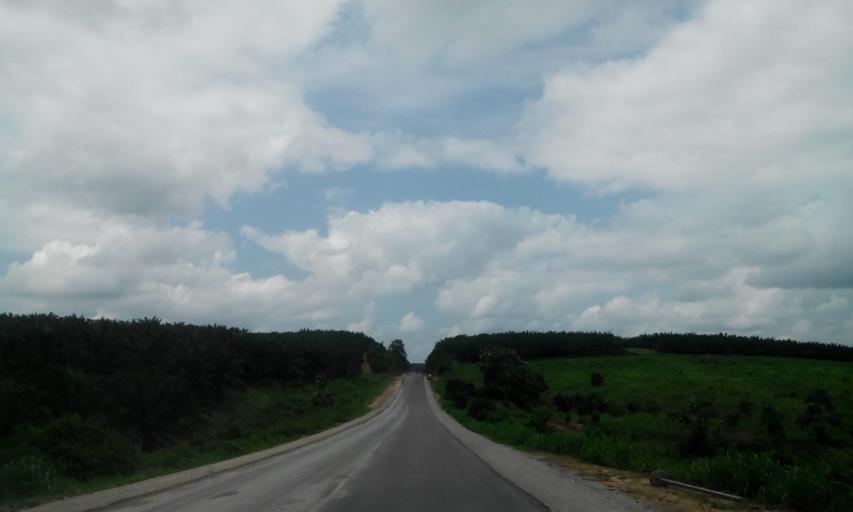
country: CI
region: Sud-Comoe
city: Mafere
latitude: 5.2989
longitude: -3.0163
